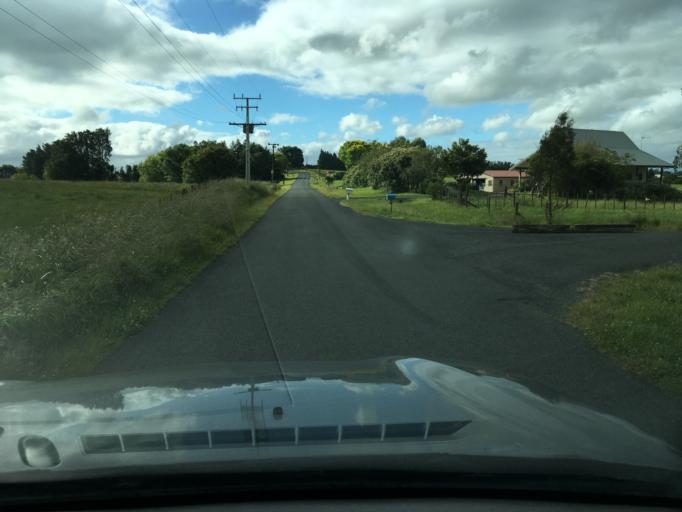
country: NZ
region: Waikato
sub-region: Hamilton City
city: Hamilton
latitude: -37.8273
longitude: 175.1791
